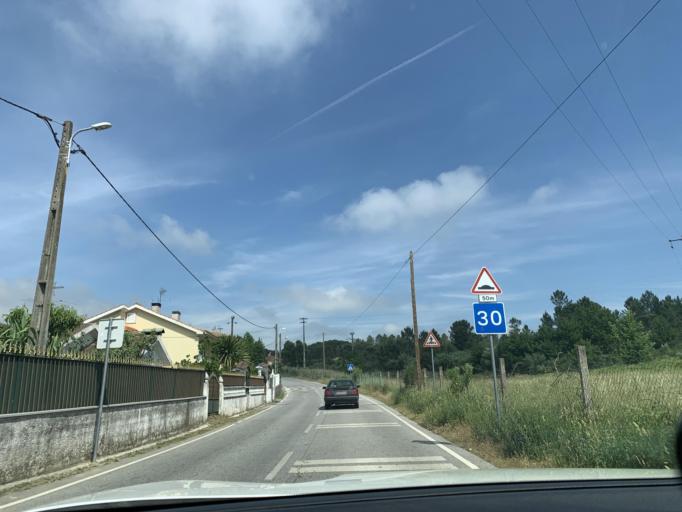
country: PT
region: Viseu
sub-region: Viseu
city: Viseu
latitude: 40.6405
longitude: -7.9359
